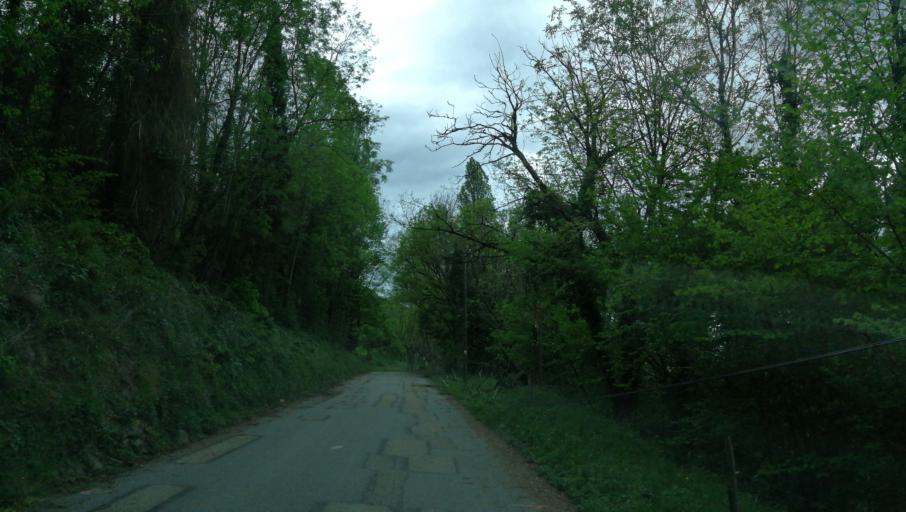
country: FR
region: Rhone-Alpes
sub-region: Departement de la Savoie
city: Chatillon
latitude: 45.7537
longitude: 5.8362
